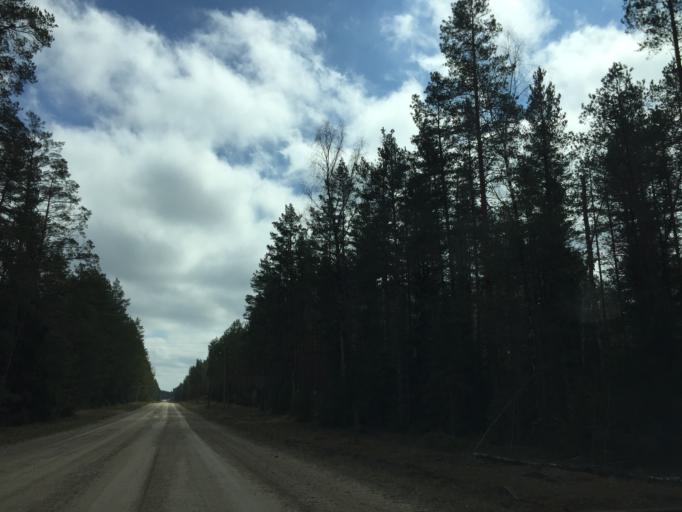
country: EE
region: Valgamaa
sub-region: Valga linn
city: Valga
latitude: 57.6609
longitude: 26.2022
